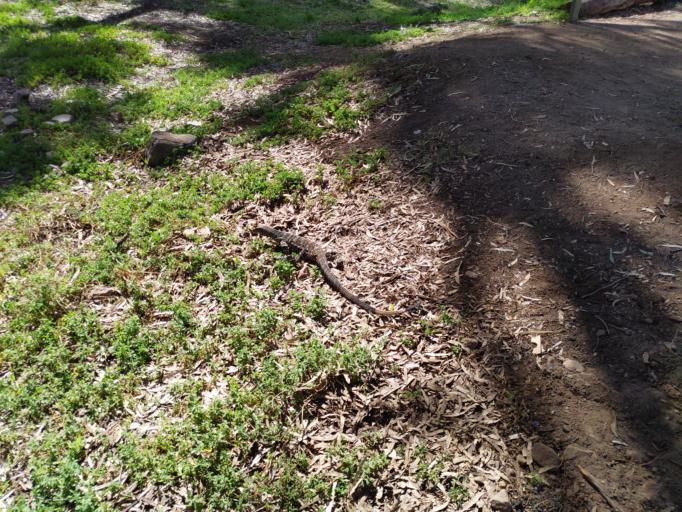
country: AU
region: South Australia
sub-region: Port Pirie City and Dists
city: Port Pirie
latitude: -32.8390
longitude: 138.0381
